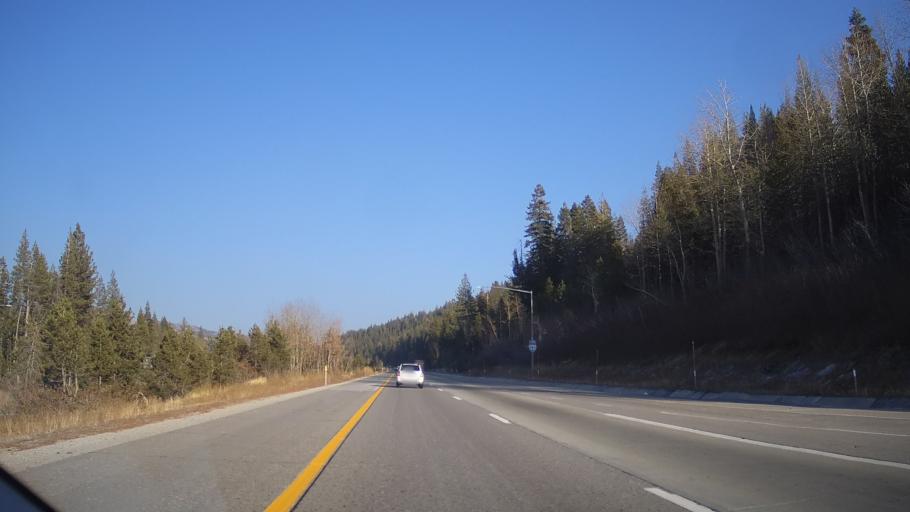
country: US
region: California
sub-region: Nevada County
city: Truckee
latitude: 39.3148
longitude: -120.4425
